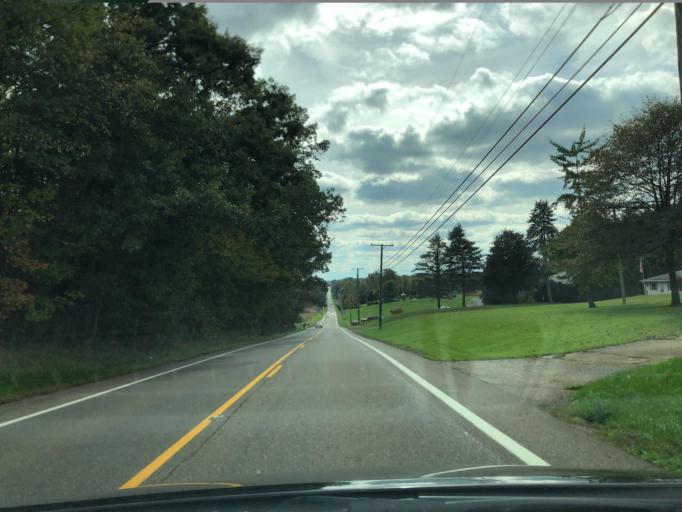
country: US
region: Ohio
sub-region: Stark County
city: Brewster
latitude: 40.7401
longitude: -81.5959
